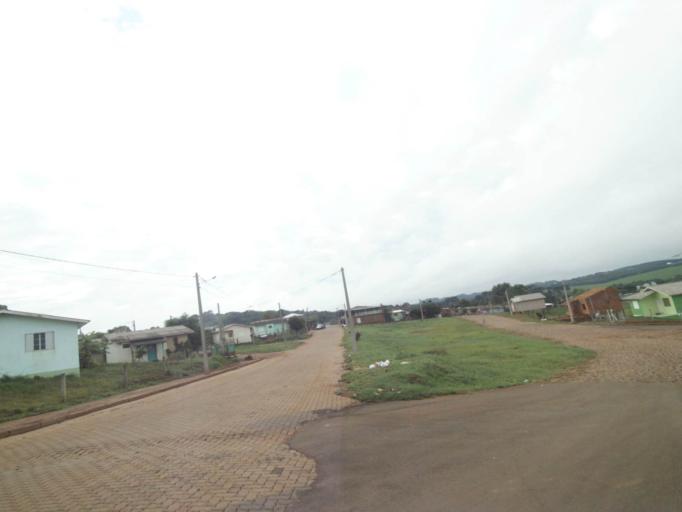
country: BR
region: Rio Grande do Sul
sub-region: Lagoa Vermelha
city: Lagoa Vermelha
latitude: -28.2275
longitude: -51.5191
